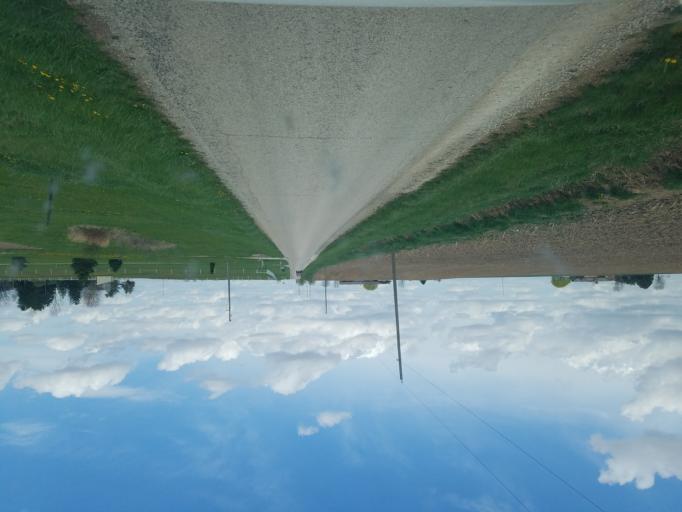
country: US
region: Ohio
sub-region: Crawford County
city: Bucyrus
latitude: 40.9043
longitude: -82.9881
